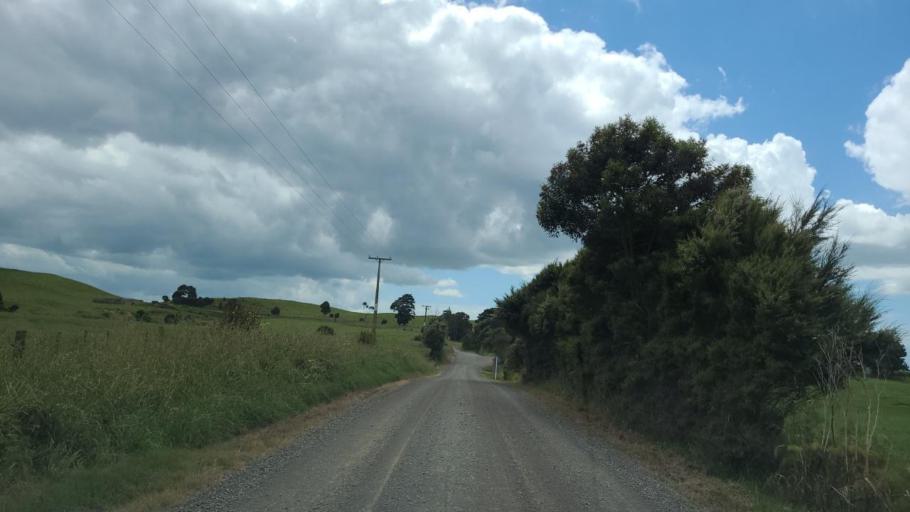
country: NZ
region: Waikato
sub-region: Hauraki District
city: Ngatea
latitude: -37.4503
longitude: 175.4991
